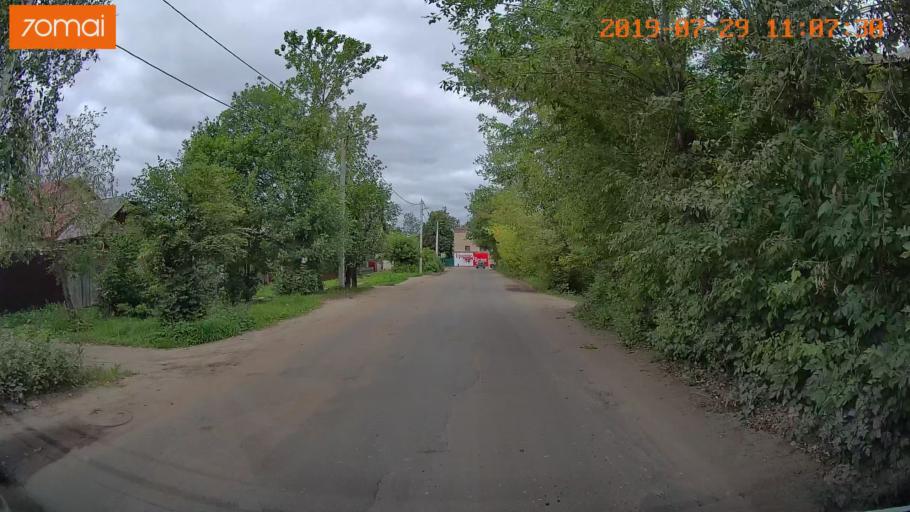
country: RU
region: Ivanovo
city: Bogorodskoye
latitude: 56.9944
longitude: 41.0373
